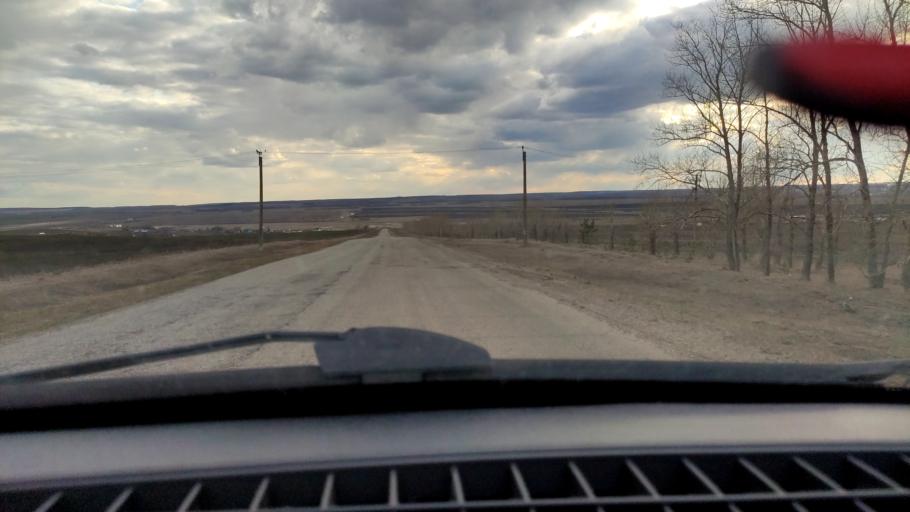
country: RU
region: Bashkortostan
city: Karmaskaly
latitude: 54.2991
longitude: 55.9228
